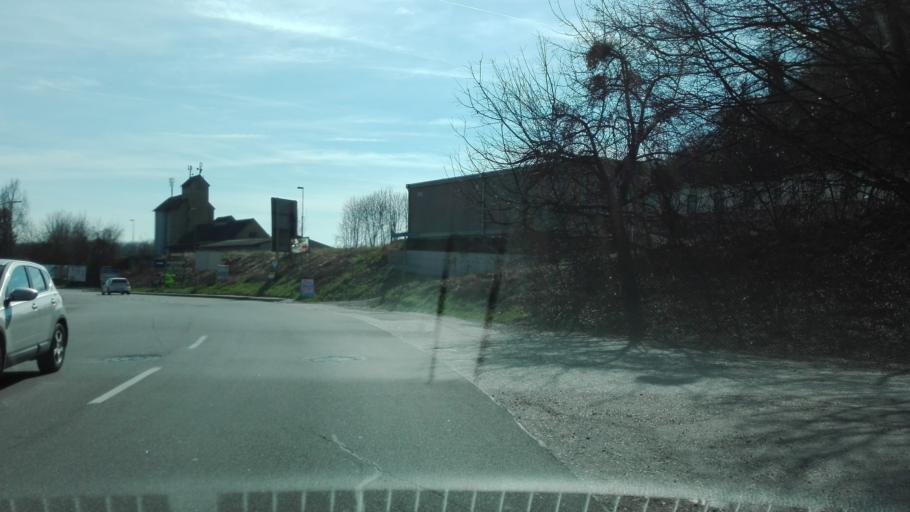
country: AT
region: Lower Austria
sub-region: Politischer Bezirk Amstetten
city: Ennsdorf
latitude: 48.2432
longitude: 14.5335
